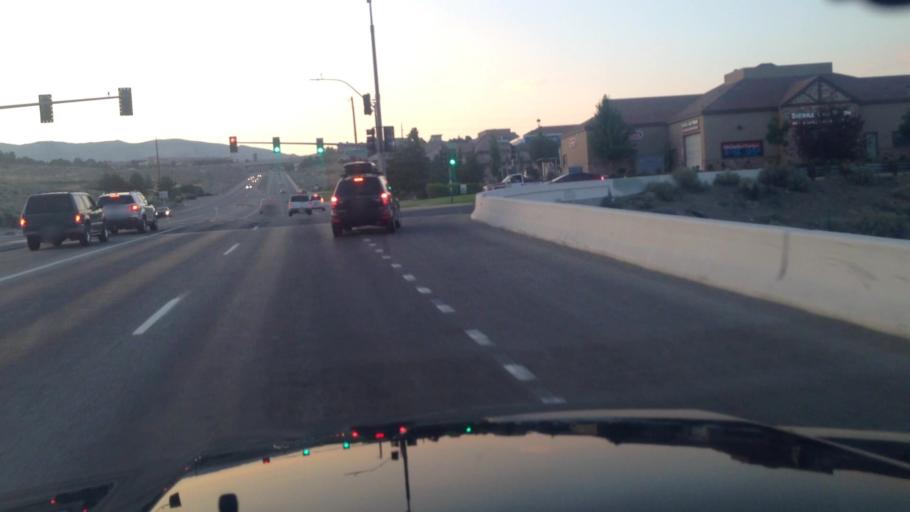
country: US
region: Nevada
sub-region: Washoe County
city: Reno
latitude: 39.5121
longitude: -119.8589
